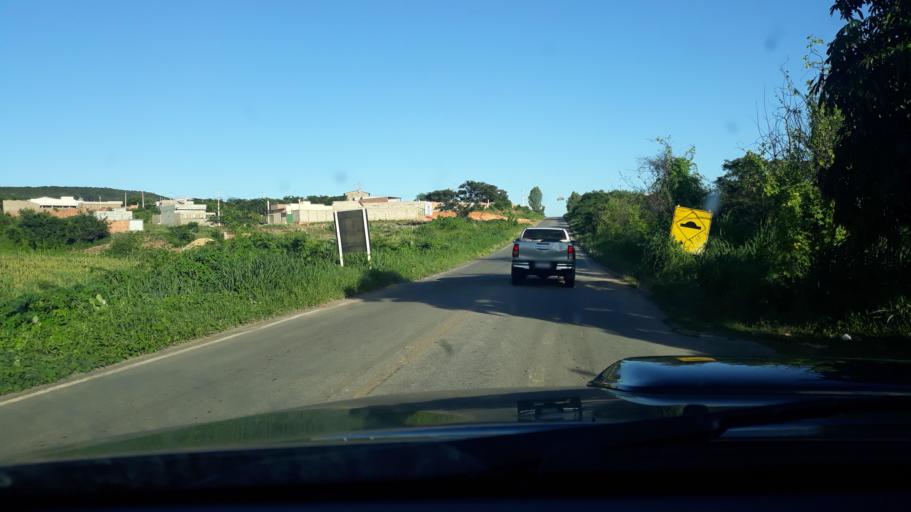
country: BR
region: Bahia
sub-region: Riacho De Santana
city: Riacho de Santana
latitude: -13.7650
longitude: -42.7269
